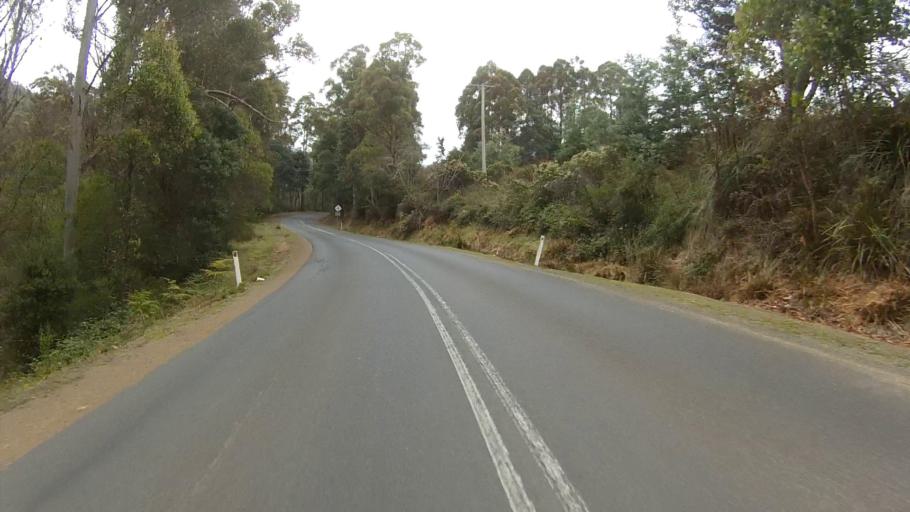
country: AU
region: Tasmania
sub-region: Huon Valley
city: Cygnet
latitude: -43.1461
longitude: 147.1536
